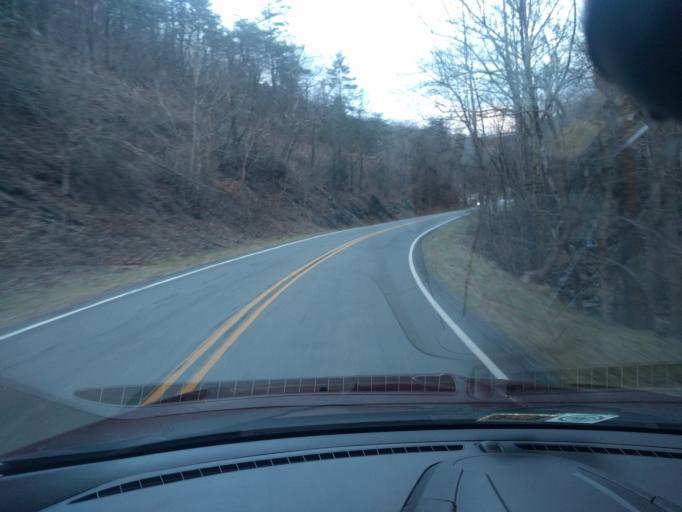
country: US
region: Virginia
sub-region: Botetourt County
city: Buchanan
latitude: 37.5203
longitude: -79.6663
